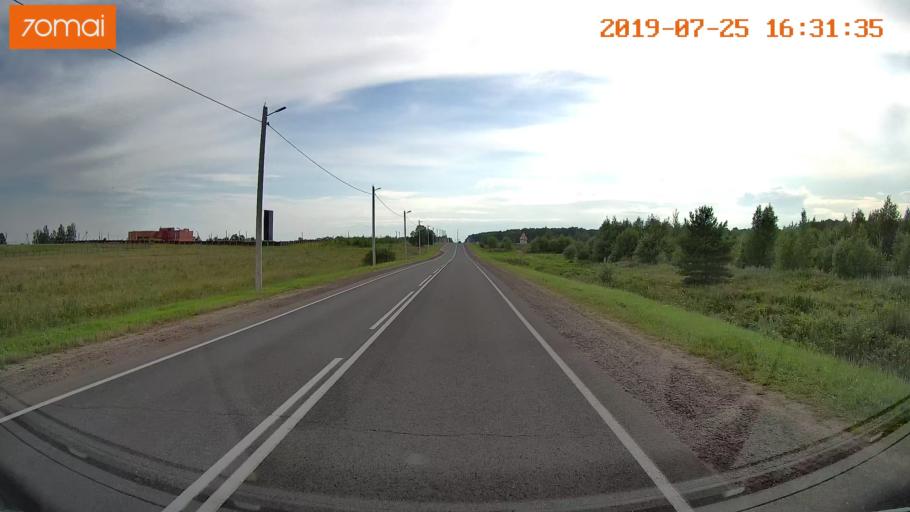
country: RU
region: Ivanovo
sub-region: Privolzhskiy Rayon
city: Ples
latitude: 57.4411
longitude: 41.4825
